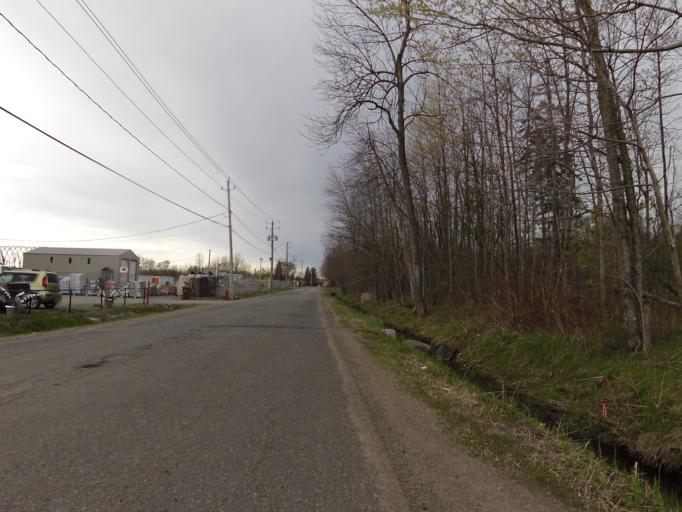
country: CA
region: Ontario
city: Hawkesbury
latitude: 45.6259
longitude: -74.5862
